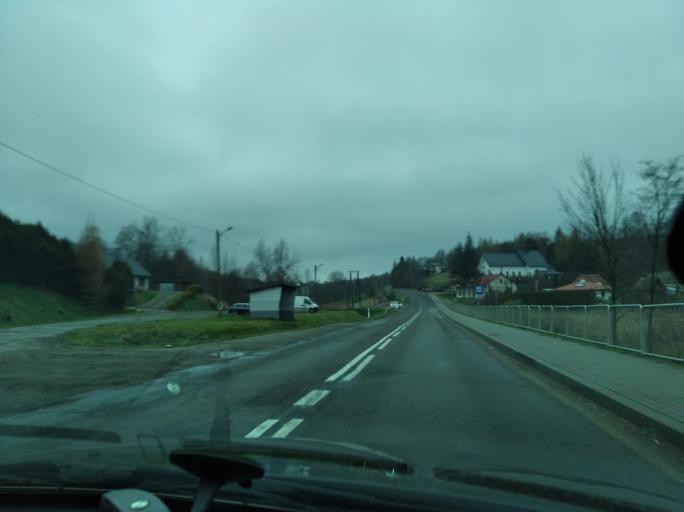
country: PL
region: Subcarpathian Voivodeship
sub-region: Powiat przeworski
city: Jawornik Polski
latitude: 49.8789
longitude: 22.2440
